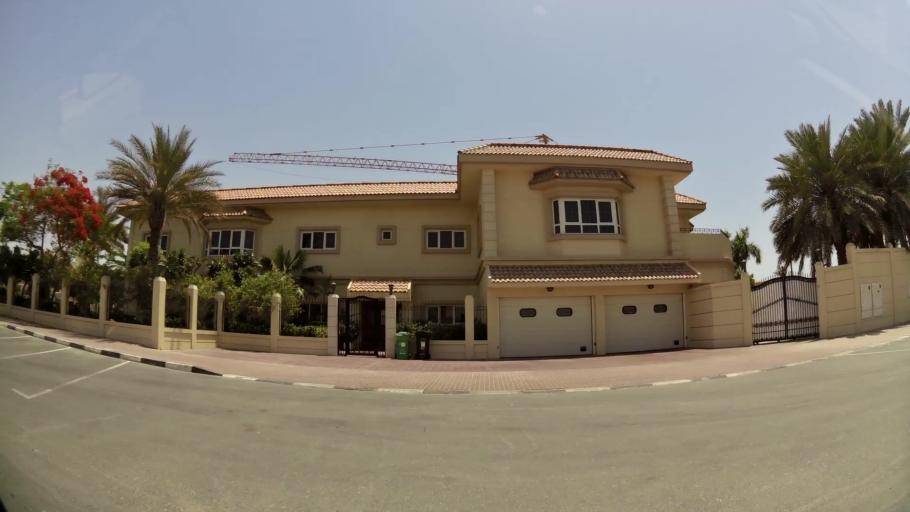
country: AE
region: Dubai
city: Dubai
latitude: 25.2245
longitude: 55.2651
